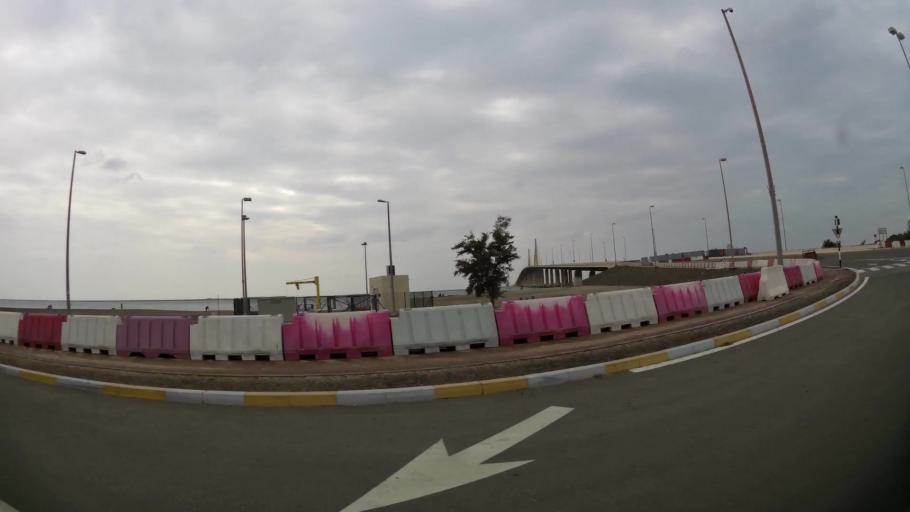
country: AE
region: Abu Dhabi
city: Abu Dhabi
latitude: 24.4300
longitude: 54.3719
